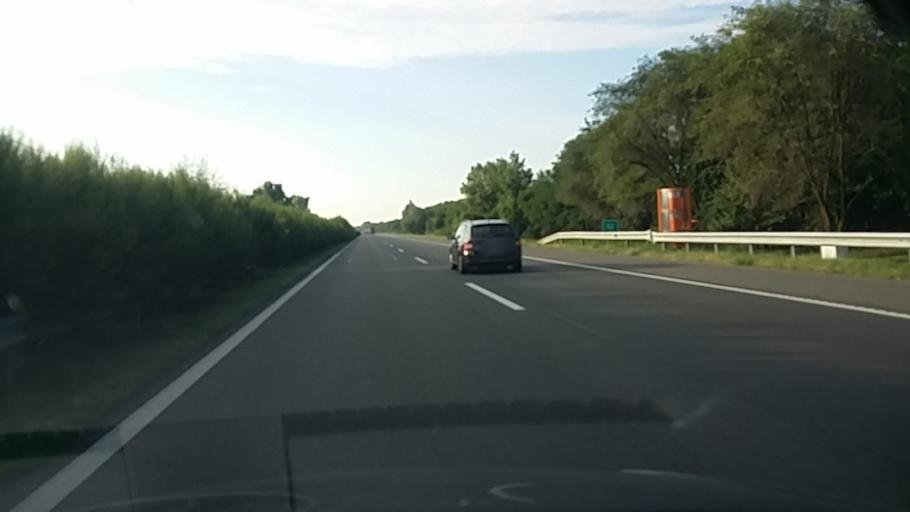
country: HU
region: Pest
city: Taborfalva
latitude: 47.0790
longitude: 19.5298
